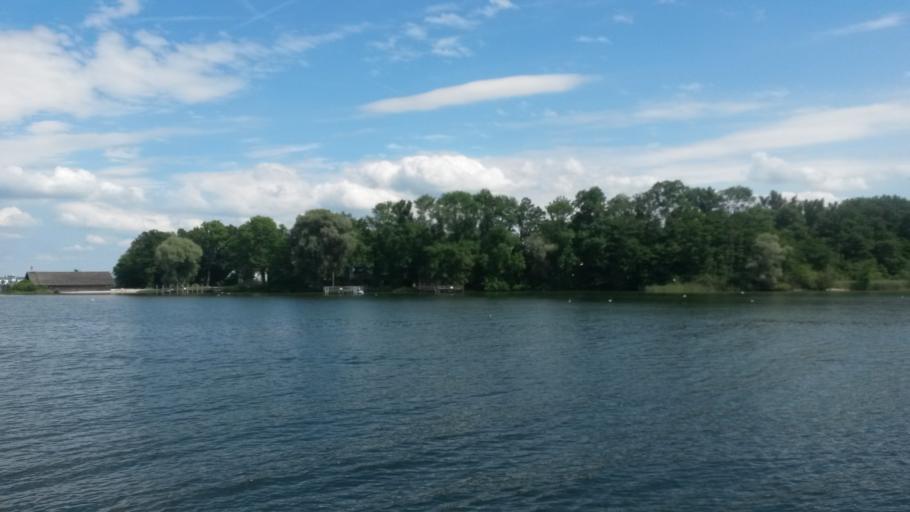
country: DE
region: Bavaria
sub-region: Upper Bavaria
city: Chiemsee
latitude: 47.8729
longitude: 12.3896
